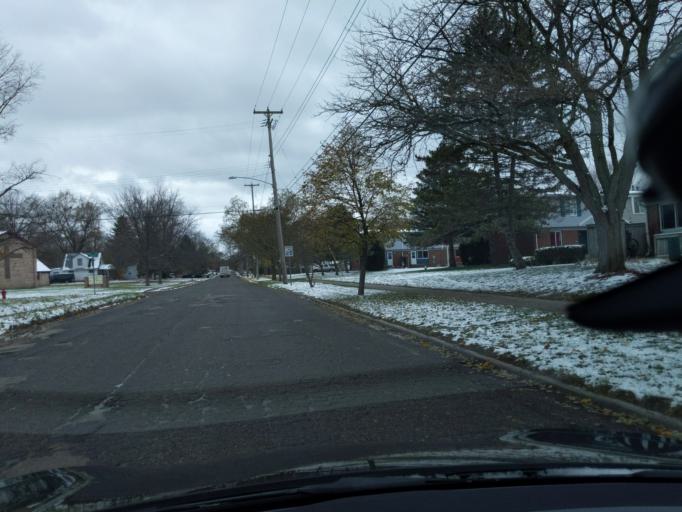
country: US
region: Michigan
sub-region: Ingham County
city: Lansing
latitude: 42.6867
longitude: -84.5855
